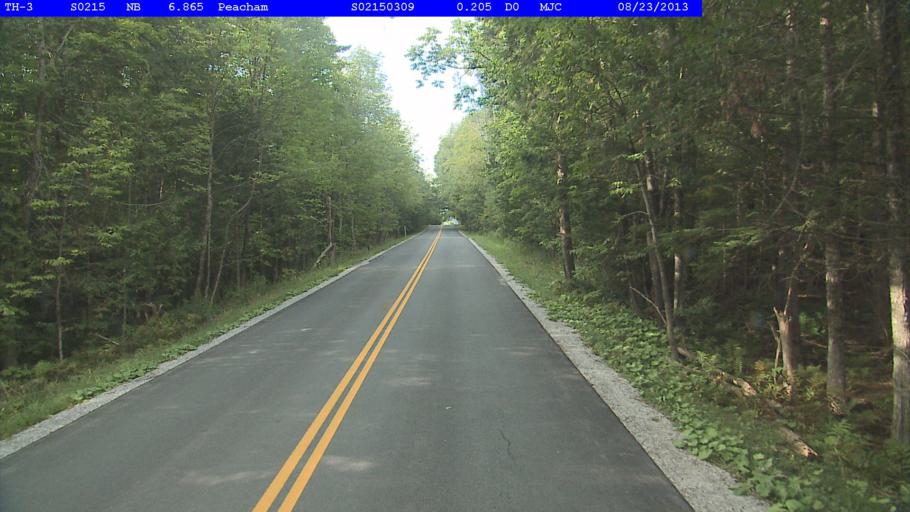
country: US
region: Vermont
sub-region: Caledonia County
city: Saint Johnsbury
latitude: 44.3008
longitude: -72.1638
